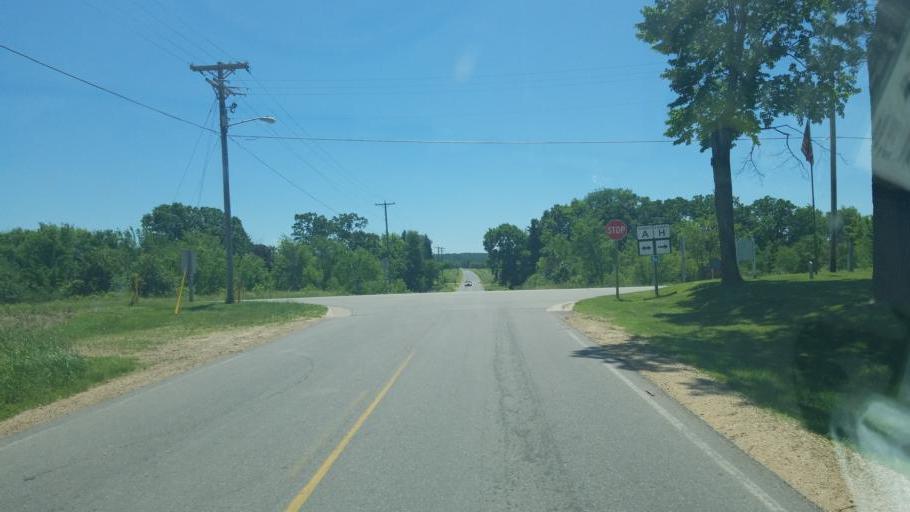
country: US
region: Wisconsin
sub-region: Juneau County
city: New Lisbon
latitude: 43.8793
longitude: -90.2620
